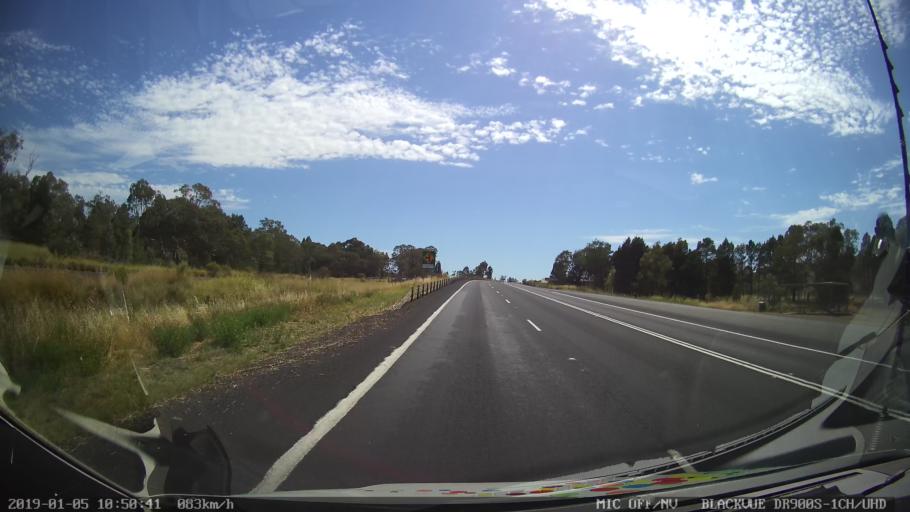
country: AU
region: New South Wales
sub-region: Warrumbungle Shire
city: Coonabarabran
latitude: -31.4274
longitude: 149.0786
